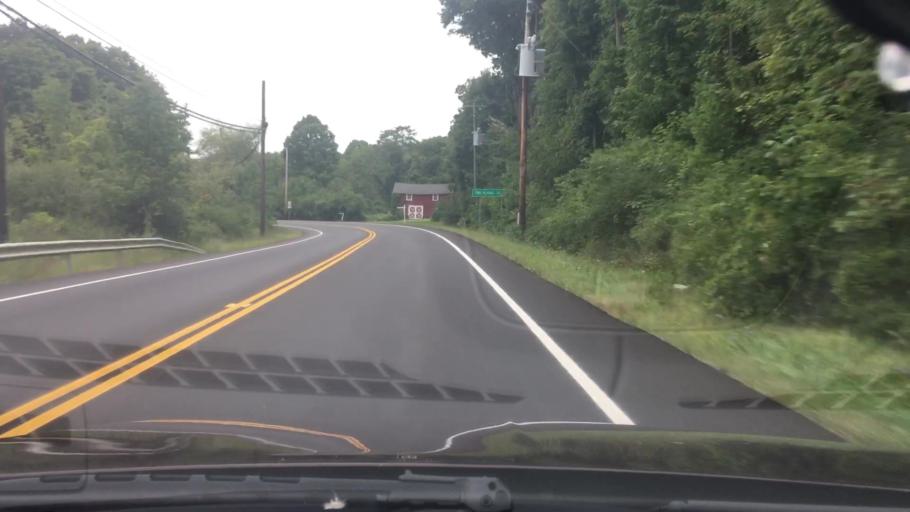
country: US
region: New York
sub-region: Dutchess County
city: Dover Plains
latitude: 41.8453
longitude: -73.5781
